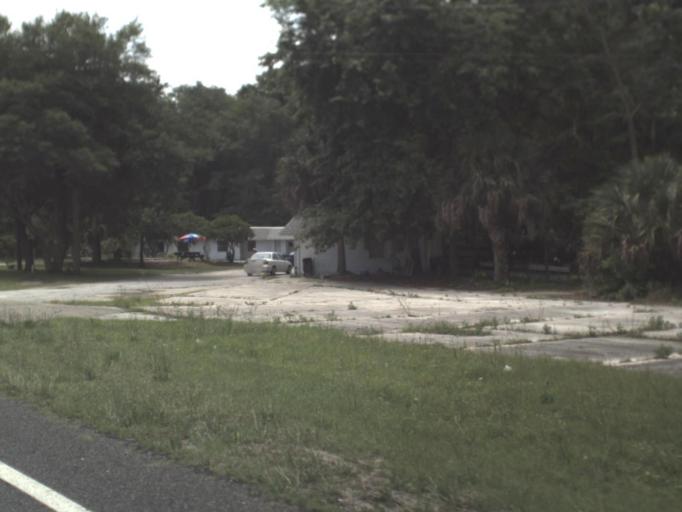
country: US
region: Florida
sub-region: Nassau County
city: Hilliard
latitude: 30.6492
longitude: -81.8731
